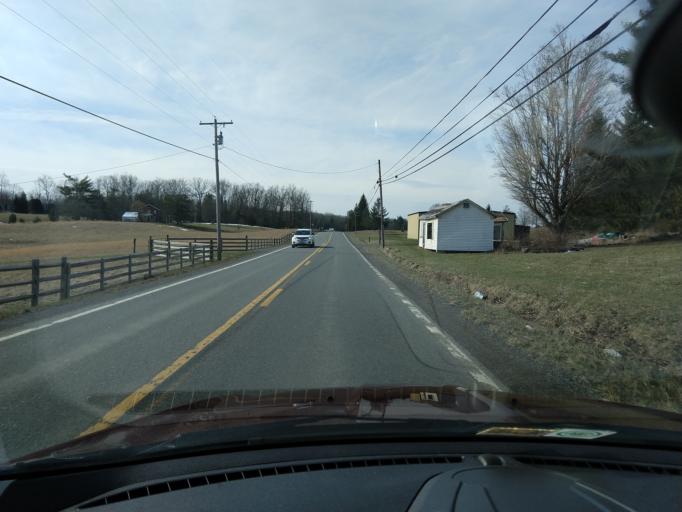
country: US
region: West Virginia
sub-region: Pocahontas County
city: Marlinton
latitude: 38.2056
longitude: -80.1087
